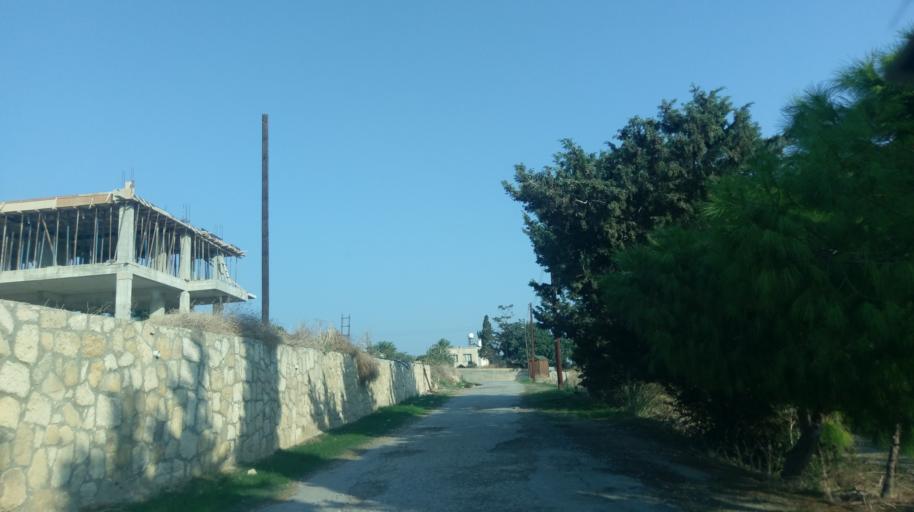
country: CY
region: Ammochostos
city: Leonarisso
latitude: 35.4773
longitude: 34.1047
